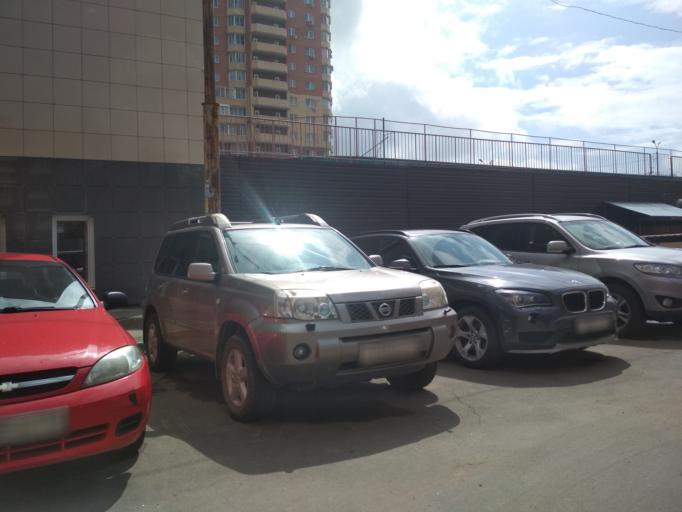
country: RU
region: Tula
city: Mendeleyevskiy
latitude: 54.1556
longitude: 37.5827
